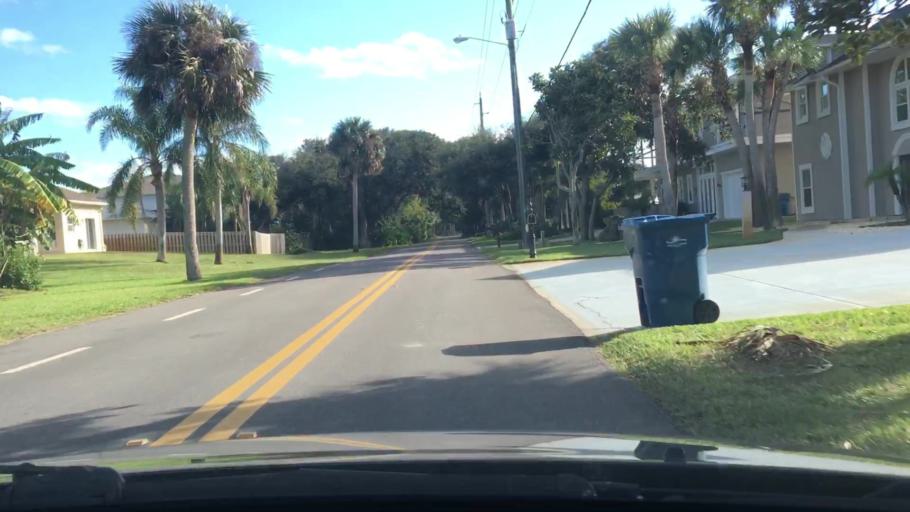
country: US
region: Florida
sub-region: Volusia County
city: Ormond-by-the-Sea
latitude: 29.3723
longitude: -81.0833
